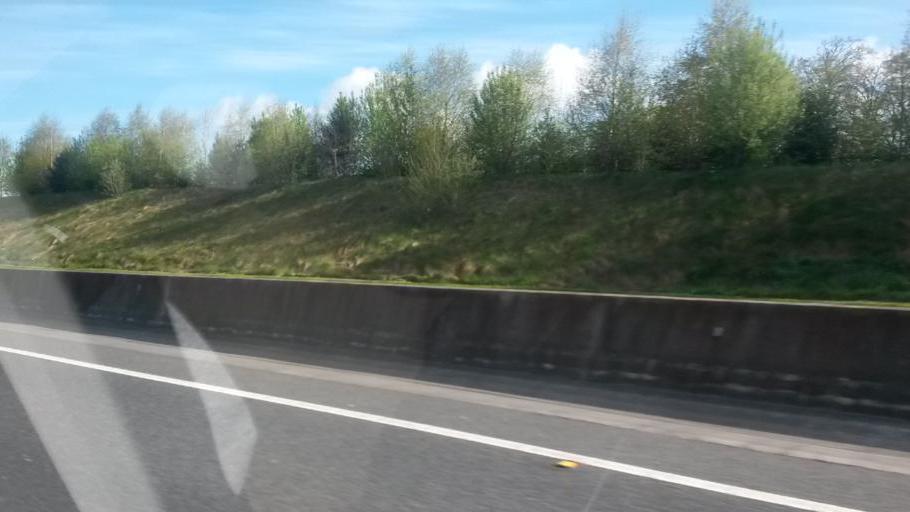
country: IE
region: Leinster
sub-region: An Mhi
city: Kells
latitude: 53.6934
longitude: -6.8260
